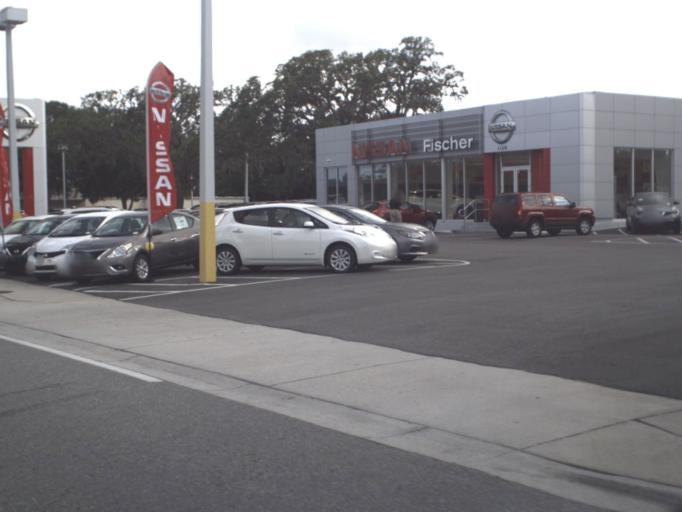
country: US
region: Florida
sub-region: Brevard County
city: Titusville
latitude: 28.6033
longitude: -80.8085
